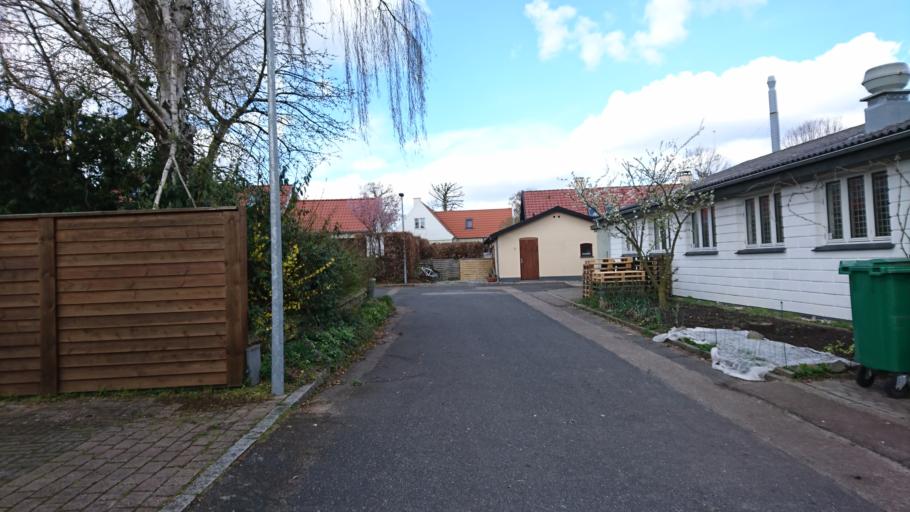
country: DK
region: Capital Region
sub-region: Egedal Kommune
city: Ganlose
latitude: 55.7926
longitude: 12.2625
